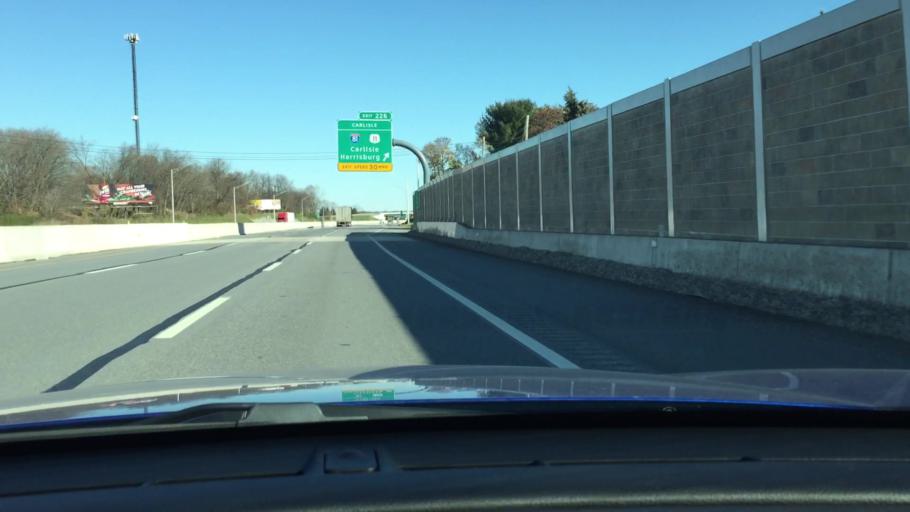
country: US
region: Pennsylvania
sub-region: Cumberland County
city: Schlusser
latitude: 40.2264
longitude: -77.1638
